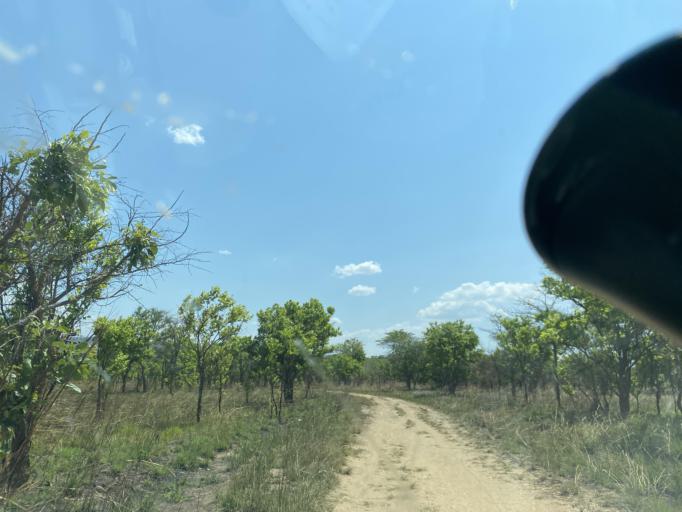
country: ZM
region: Lusaka
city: Chongwe
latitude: -15.0820
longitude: 29.5009
